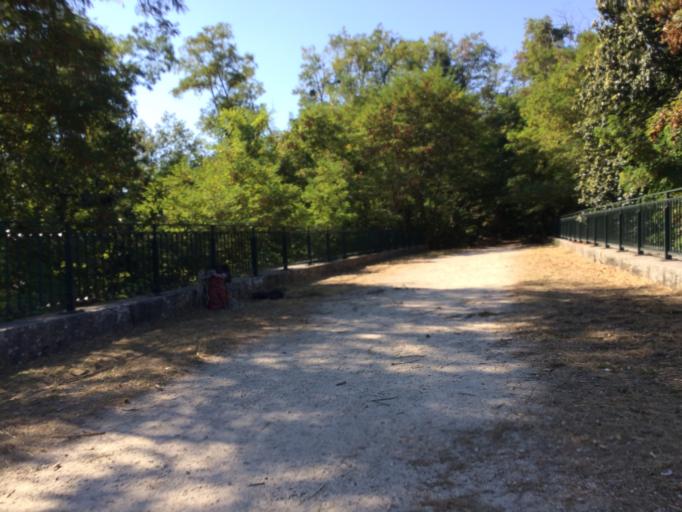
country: FR
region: Ile-de-France
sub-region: Departement de l'Essonne
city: Gometz-le-Chatel
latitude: 48.6783
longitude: 2.1521
